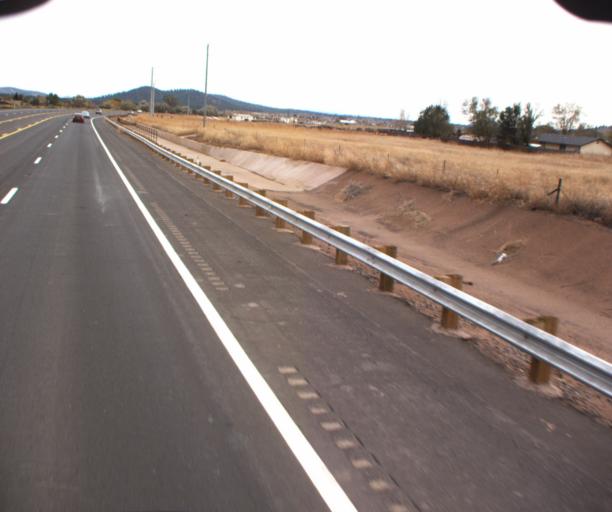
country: US
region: Arizona
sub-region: Coconino County
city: Flagstaff
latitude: 35.3260
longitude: -111.5442
